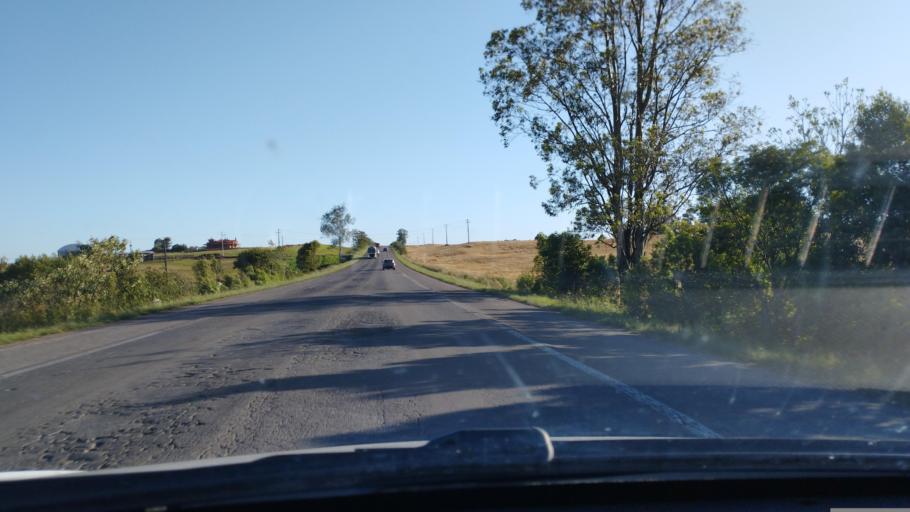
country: BR
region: Rio Grande do Sul
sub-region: Julio De Castilhos
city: Julio de Castilhos
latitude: -29.4215
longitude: -53.6724
